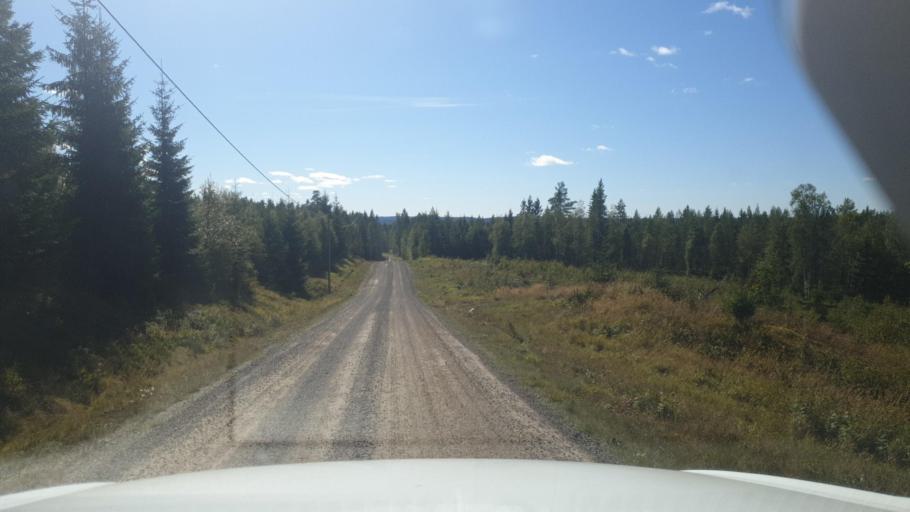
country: SE
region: Vaermland
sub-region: Eda Kommun
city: Charlottenberg
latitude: 60.1577
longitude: 12.6013
